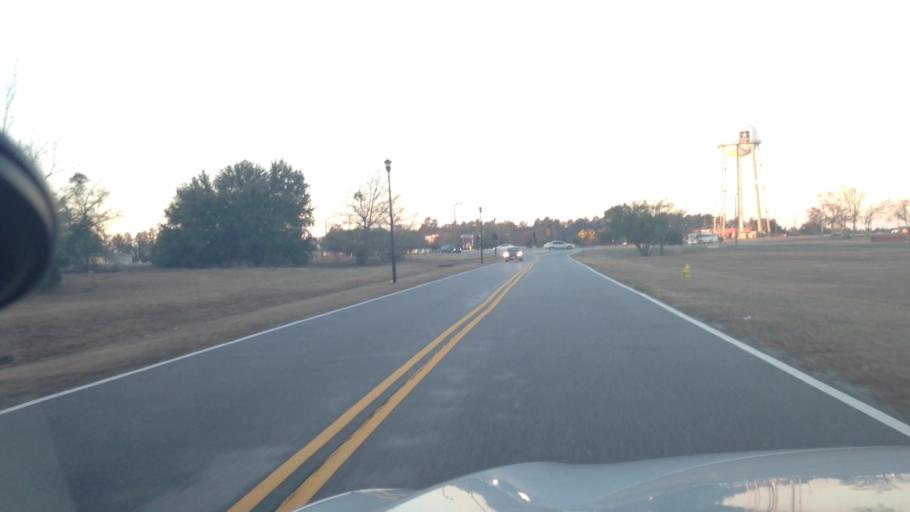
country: US
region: Georgia
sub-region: Columbia County
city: Grovetown
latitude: 33.4170
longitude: -82.1363
